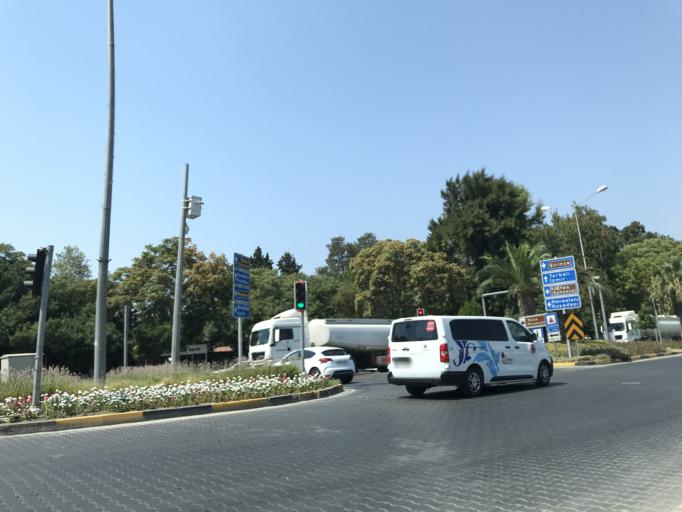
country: TR
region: Izmir
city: Selcuk
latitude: 37.9478
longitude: 27.3686
